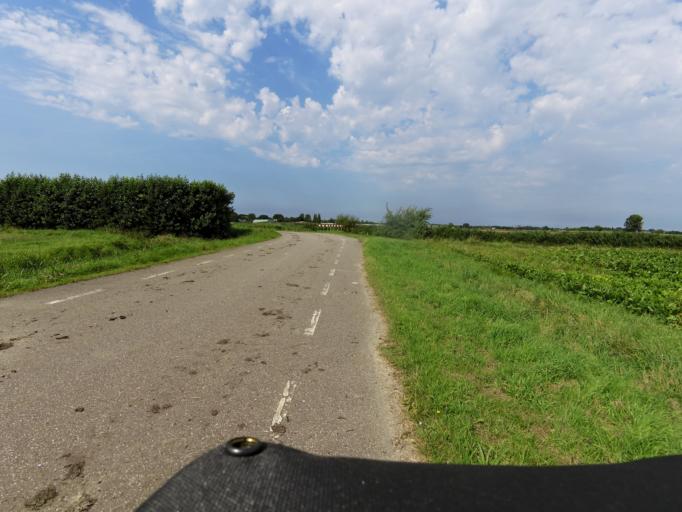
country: NL
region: South Holland
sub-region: Gemeente Binnenmaas
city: Heinenoord
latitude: 51.8134
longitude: 4.4453
